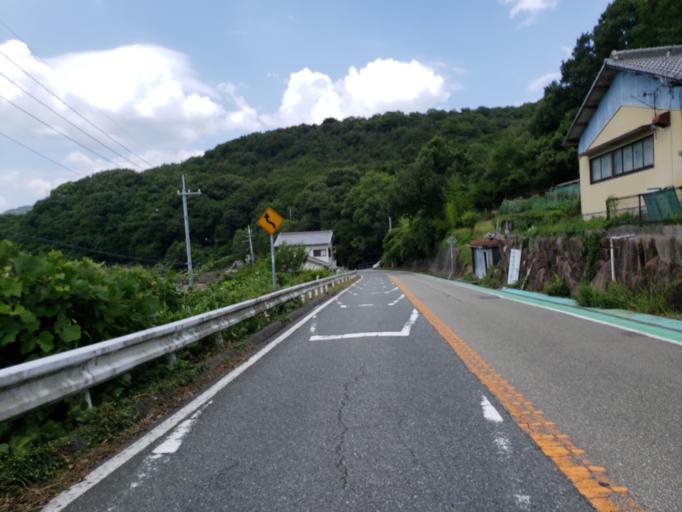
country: JP
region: Hyogo
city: Aioi
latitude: 34.7680
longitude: 134.4735
